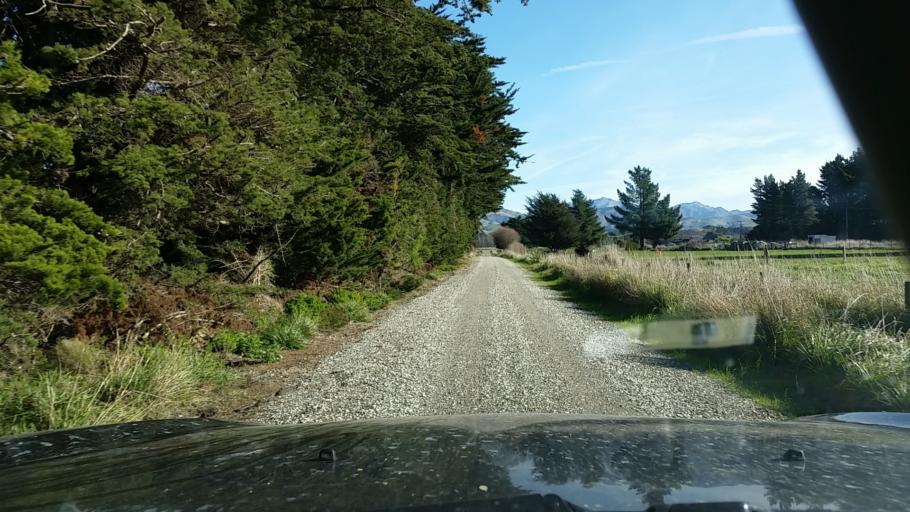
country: NZ
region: Marlborough
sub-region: Marlborough District
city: Blenheim
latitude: -41.8269
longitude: 174.1540
